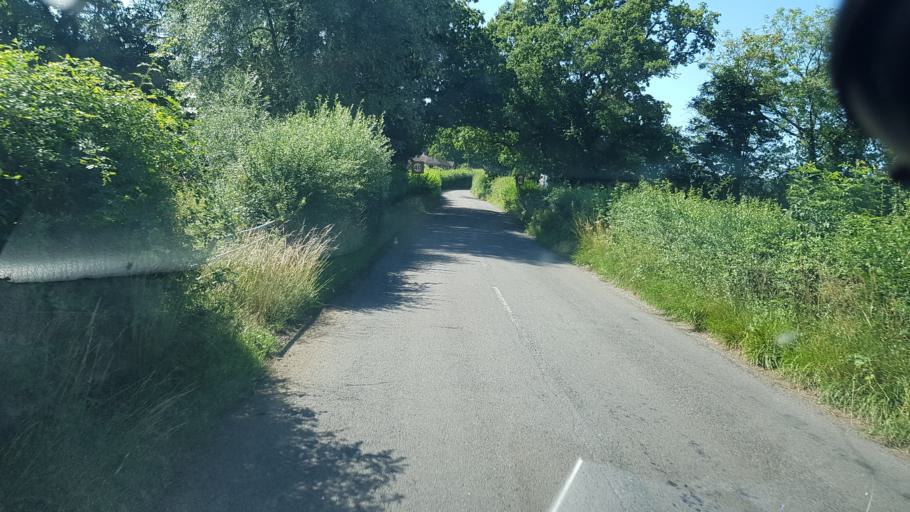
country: GB
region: England
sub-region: Kent
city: Edenbridge
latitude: 51.2221
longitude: 0.0855
